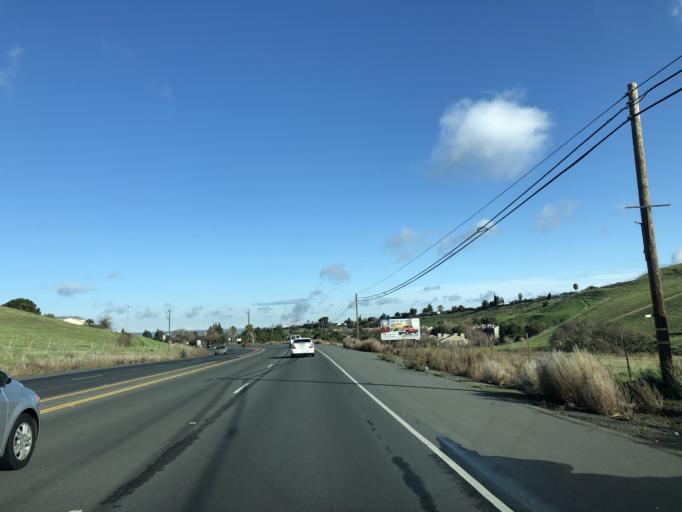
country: US
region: California
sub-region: Contra Costa County
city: Pittsburg
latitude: 37.9886
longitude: -121.8968
